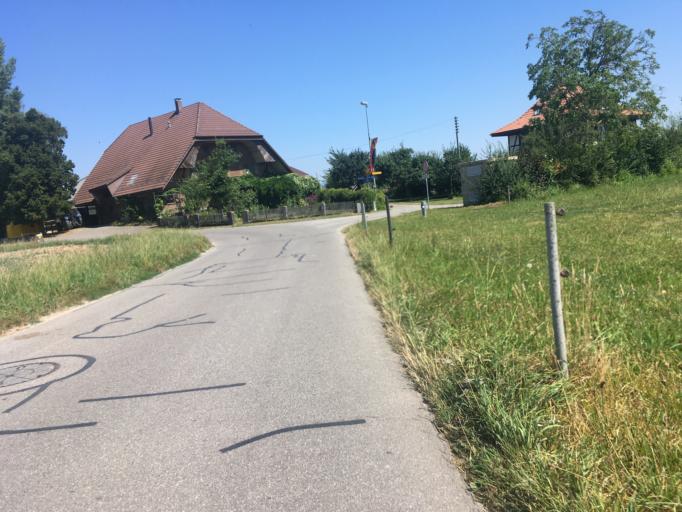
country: CH
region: Bern
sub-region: Bern-Mittelland District
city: Fraubrunnen
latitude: 47.0847
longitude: 7.5118
